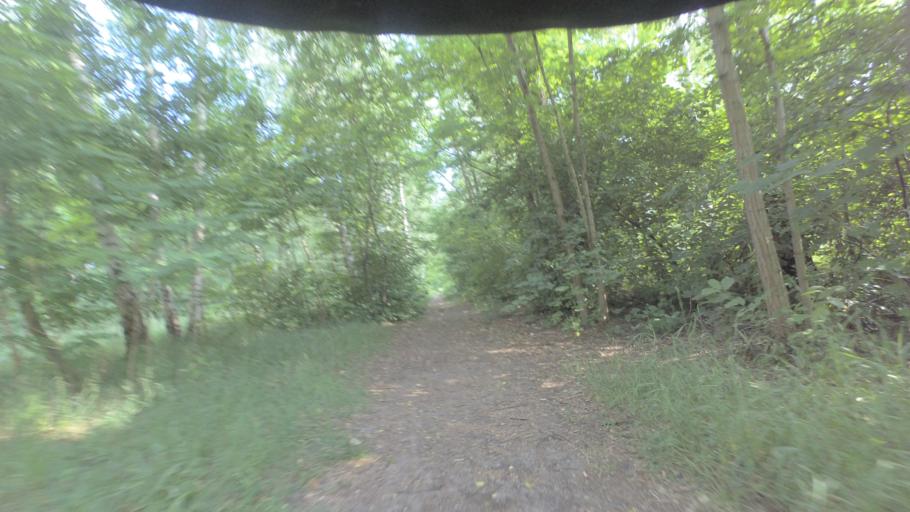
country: DE
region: Berlin
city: Lichtenrade
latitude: 52.4015
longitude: 13.4218
